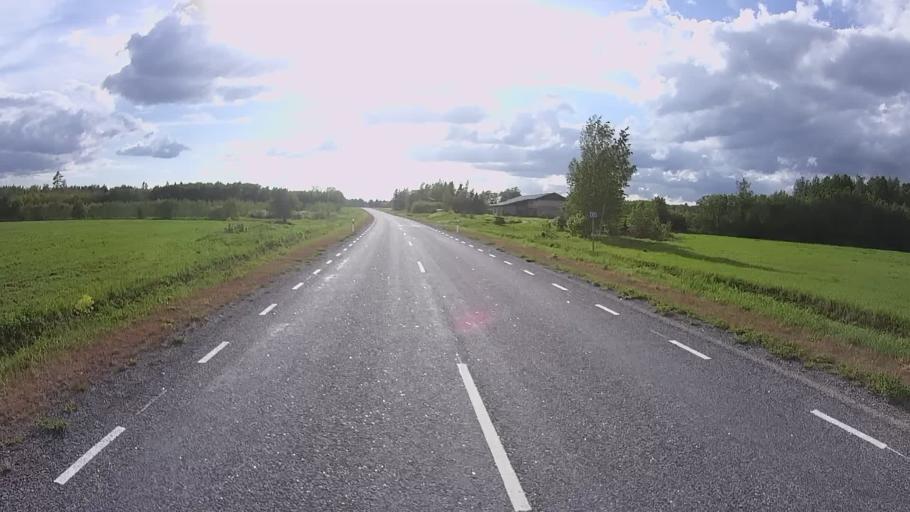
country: EE
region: Jogevamaa
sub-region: Mustvee linn
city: Mustvee
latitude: 59.0256
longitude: 27.0116
